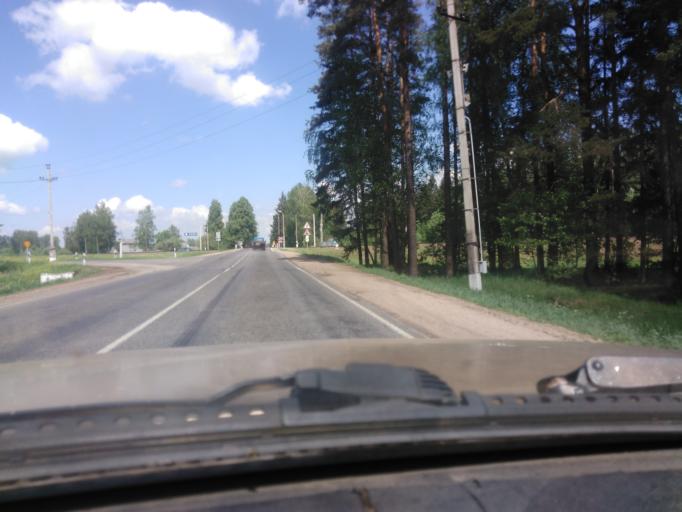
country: BY
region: Mogilev
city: Palykavichy Pyershyya
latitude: 53.9862
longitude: 30.3181
